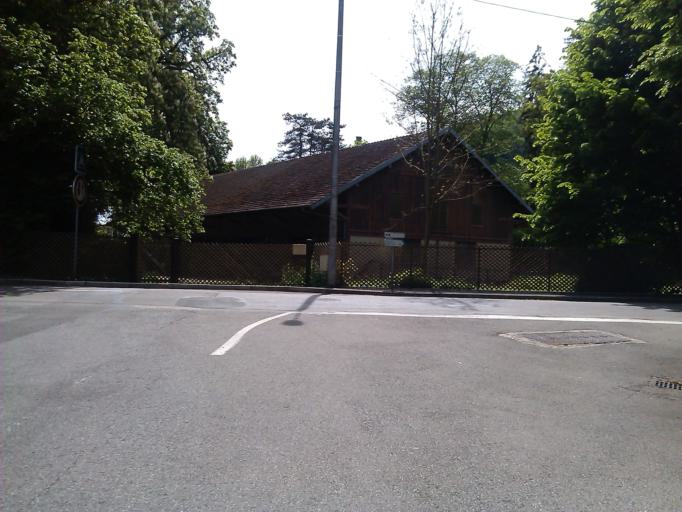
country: FR
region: Franche-Comte
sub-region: Departement du Doubs
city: Boussieres
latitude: 47.1597
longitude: 5.8878
